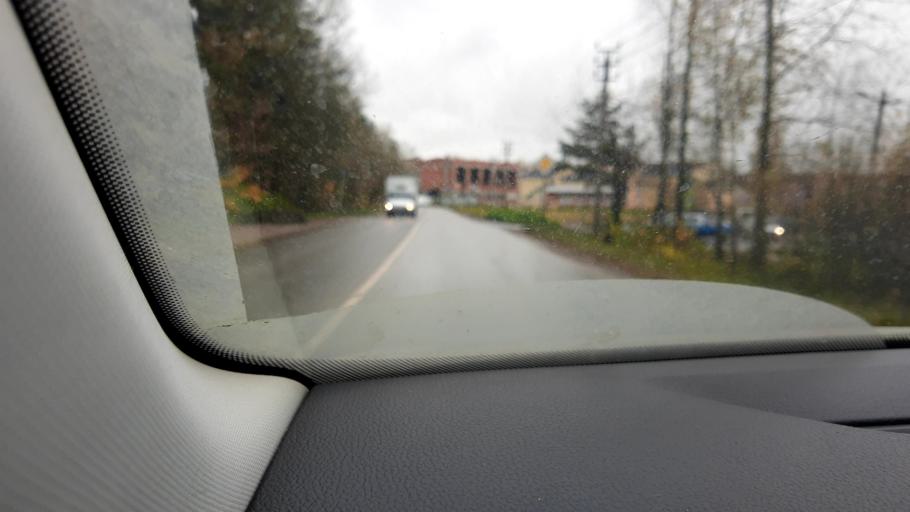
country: RU
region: Moskovskaya
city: Aprelevka
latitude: 55.5572
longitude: 37.0909
